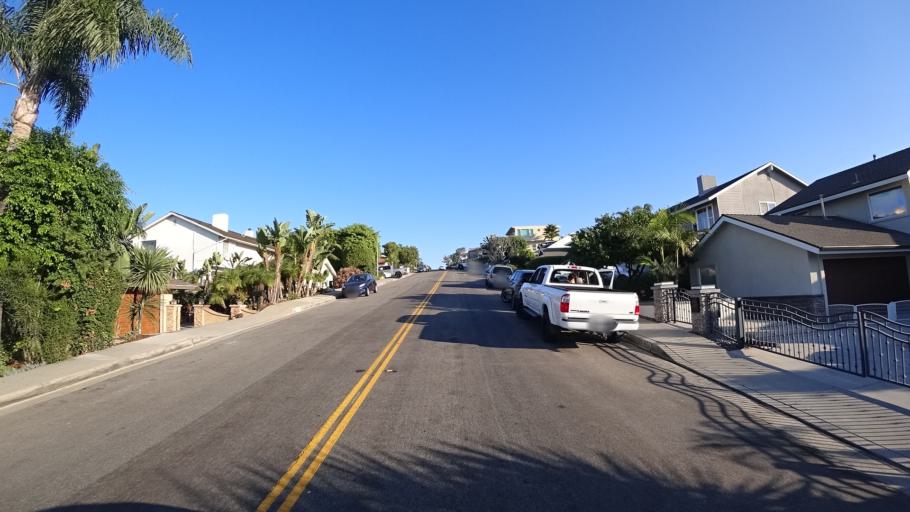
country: US
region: California
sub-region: Orange County
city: San Clemente
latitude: 33.4253
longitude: -117.6003
